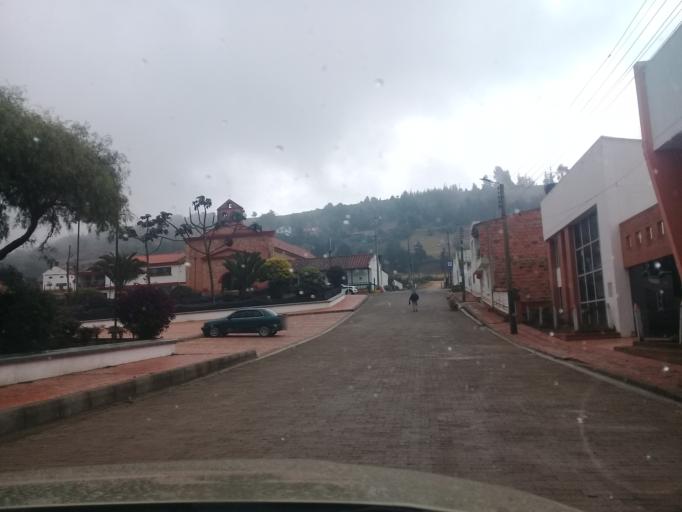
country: CO
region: Boyaca
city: Siachoque
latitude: 5.5571
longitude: -73.2835
